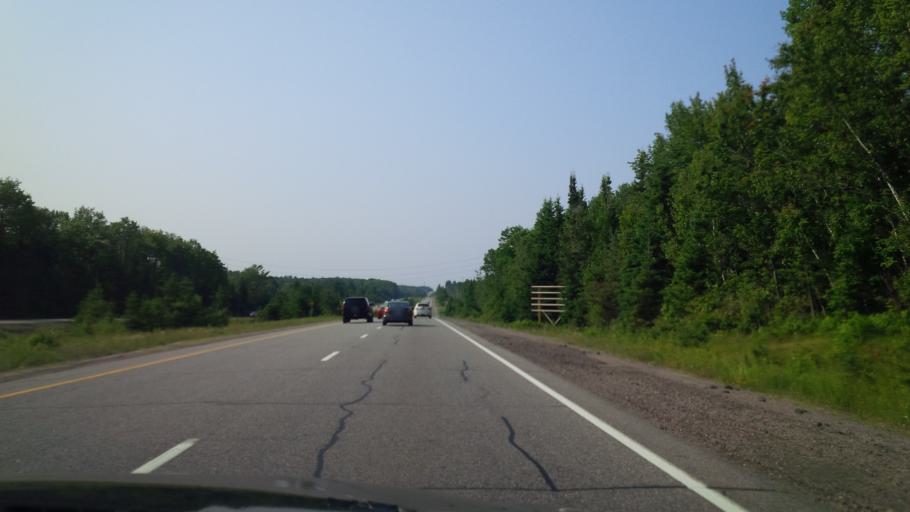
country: CA
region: Ontario
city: Bracebridge
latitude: 45.1871
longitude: -79.3129
